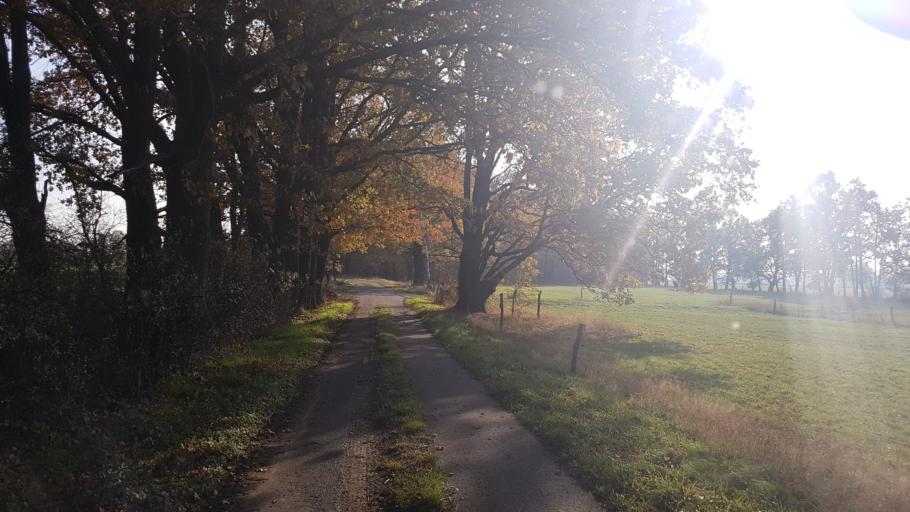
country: DE
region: Brandenburg
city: Falkenberg
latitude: 51.6236
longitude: 13.2946
